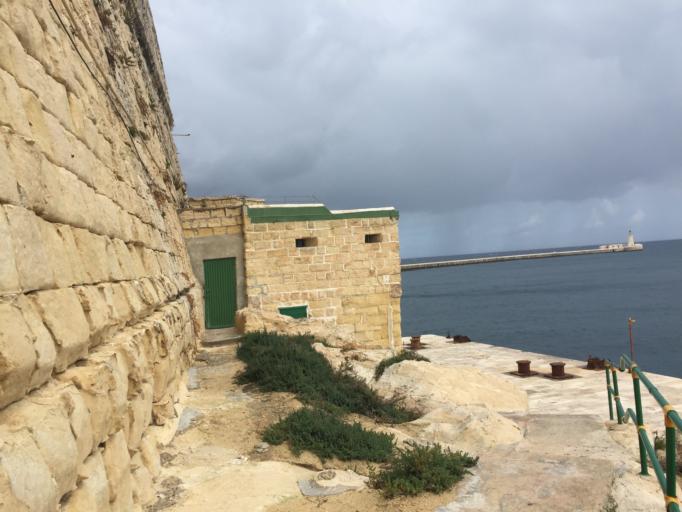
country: MT
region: Il-Belt Valletta
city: Valletta
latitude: 35.9001
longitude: 14.5190
